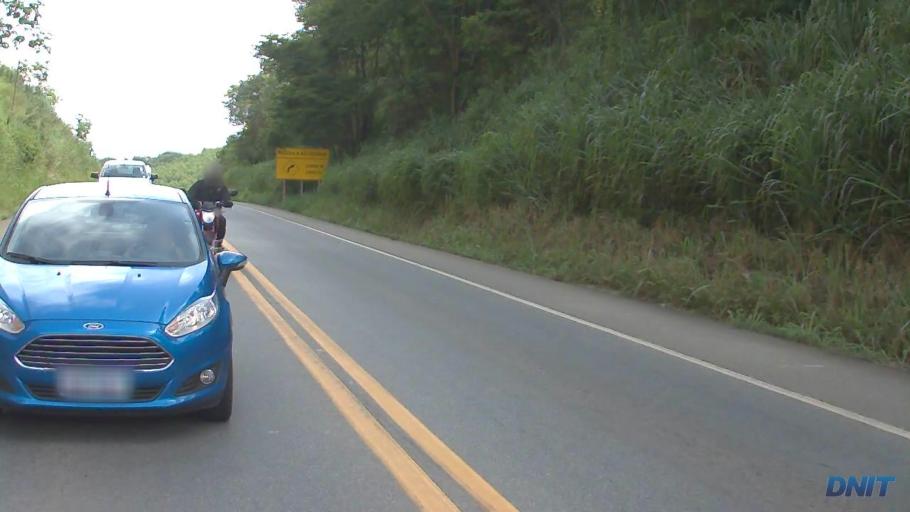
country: BR
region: Minas Gerais
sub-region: Ipaba
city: Ipaba
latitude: -19.3602
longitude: -42.4447
